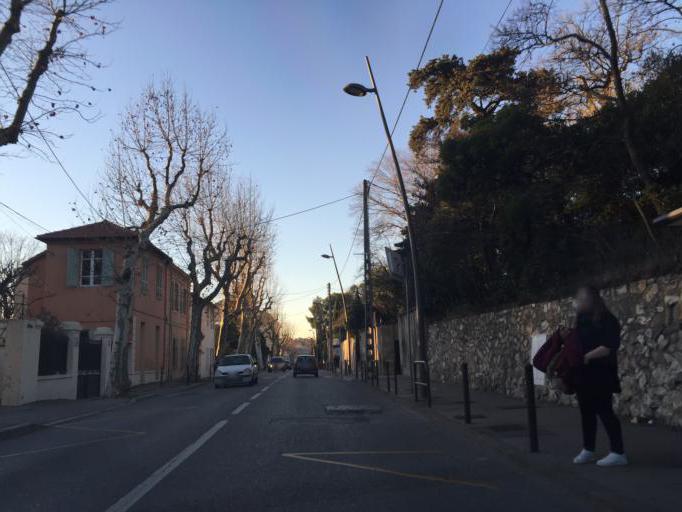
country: FR
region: Provence-Alpes-Cote d'Azur
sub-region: Departement des Bouches-du-Rhone
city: Aix-en-Provence
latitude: 43.5212
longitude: 5.4589
